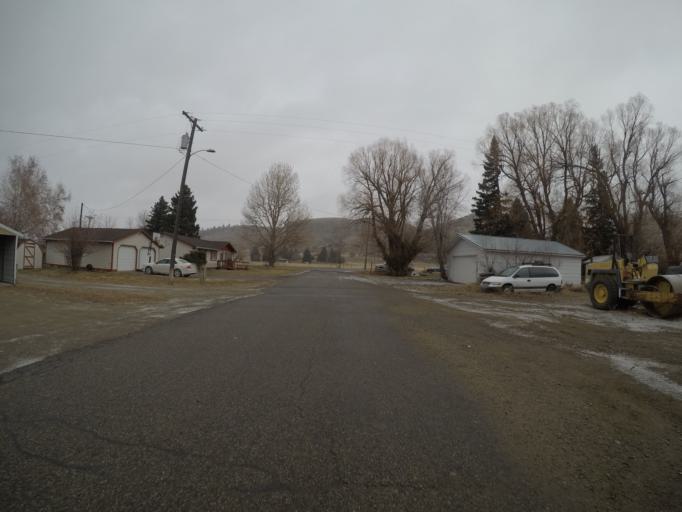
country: US
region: Montana
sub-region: Stillwater County
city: Absarokee
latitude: 45.5235
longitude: -109.4394
